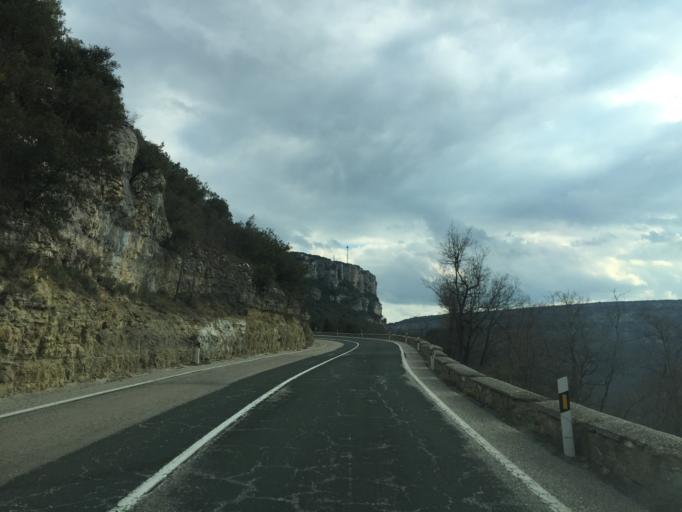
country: ES
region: Cantabria
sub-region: Provincia de Cantabria
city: San Martin de Elines
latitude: 42.8156
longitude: -3.7721
